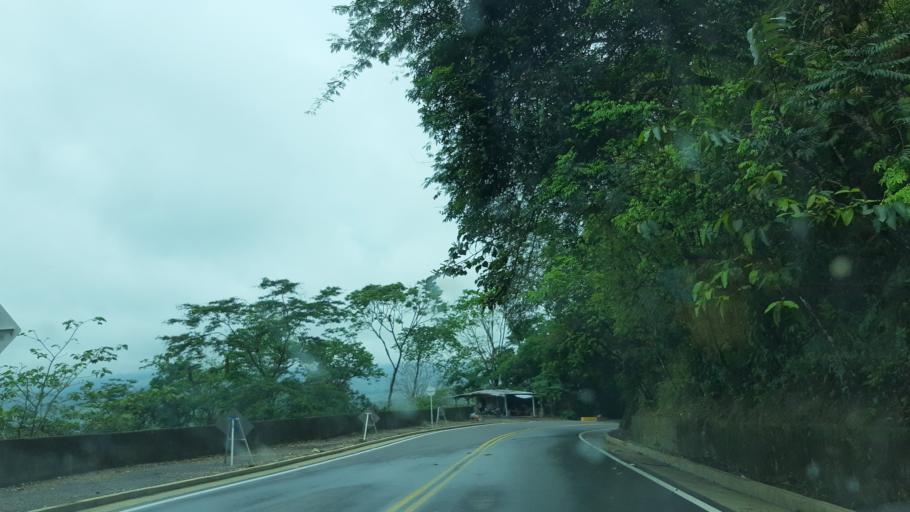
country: CO
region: Casanare
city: Sabanalarga
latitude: 4.7627
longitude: -73.0284
